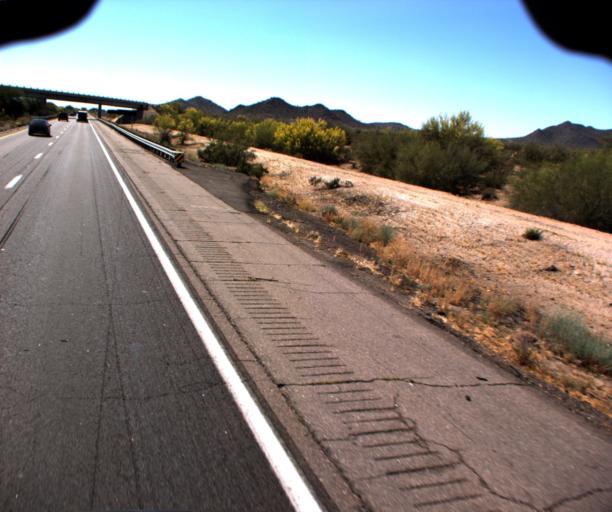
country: US
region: Arizona
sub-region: Pinal County
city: Sacaton
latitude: 33.0507
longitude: -111.7905
